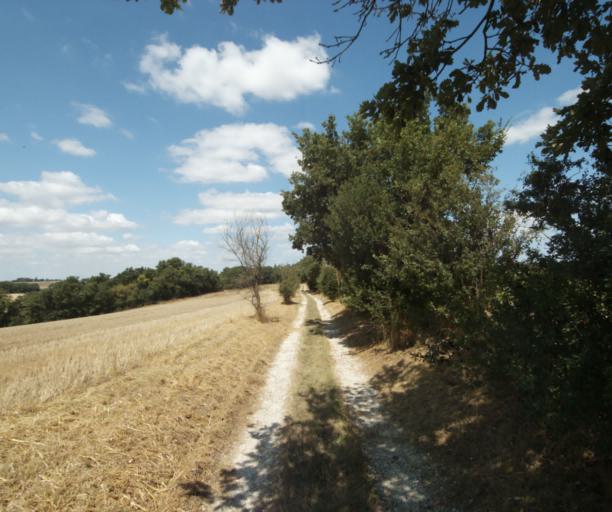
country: FR
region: Midi-Pyrenees
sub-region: Departement de la Haute-Garonne
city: Saint-Felix-Lauragais
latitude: 43.4696
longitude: 1.8584
